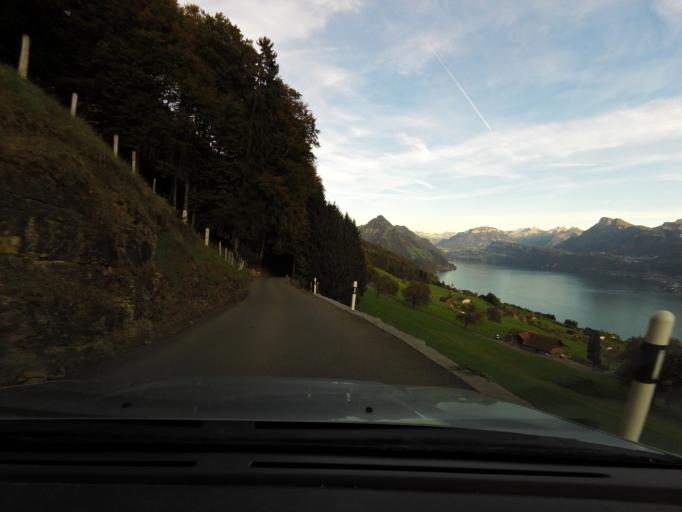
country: CH
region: Nidwalden
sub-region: Nidwalden
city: Ennetburgen
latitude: 46.9966
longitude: 8.4107
